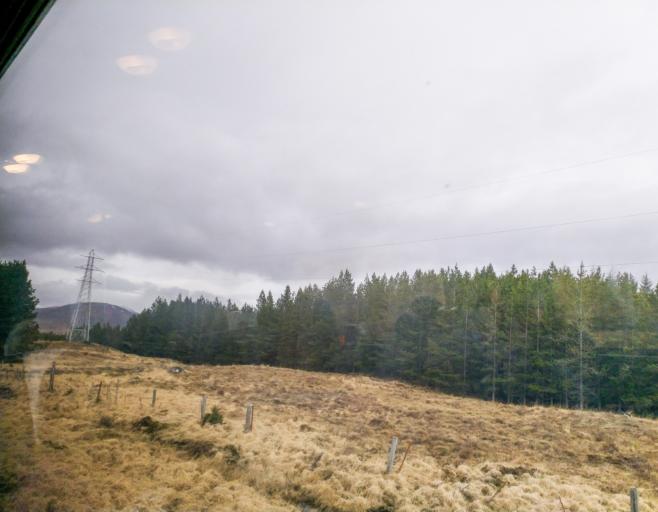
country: GB
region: Scotland
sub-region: Highland
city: Spean Bridge
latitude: 56.6648
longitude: -4.5644
